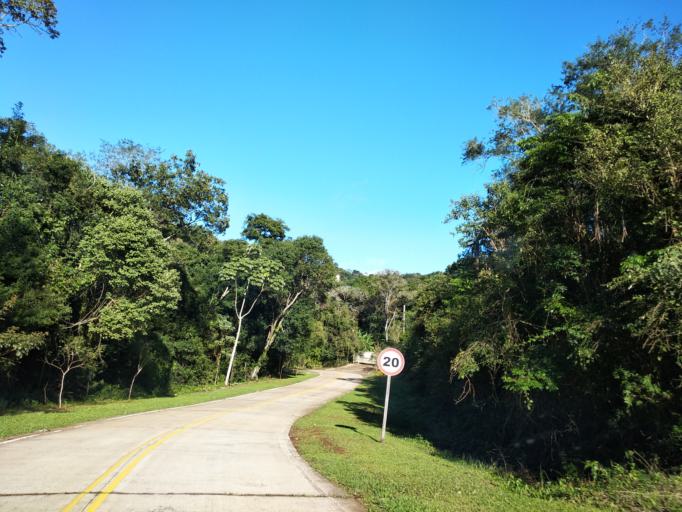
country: AR
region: Misiones
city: Cerro Cora
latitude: -27.4530
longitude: -55.5654
